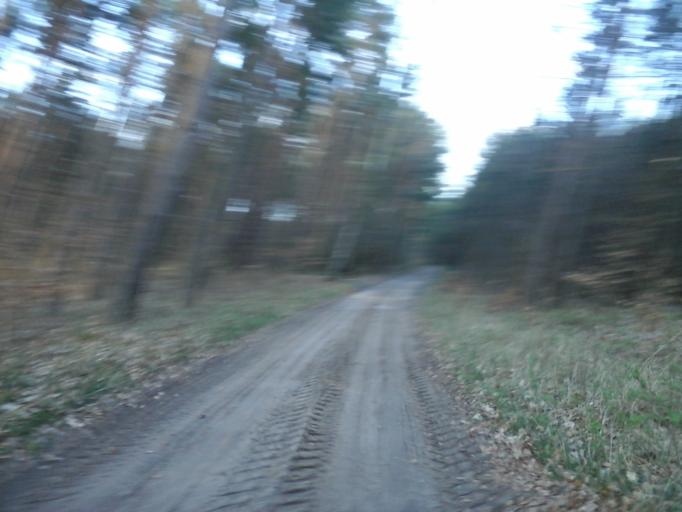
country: PL
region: West Pomeranian Voivodeship
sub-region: Powiat choszczenski
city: Bierzwnik
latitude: 53.0087
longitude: 15.6392
